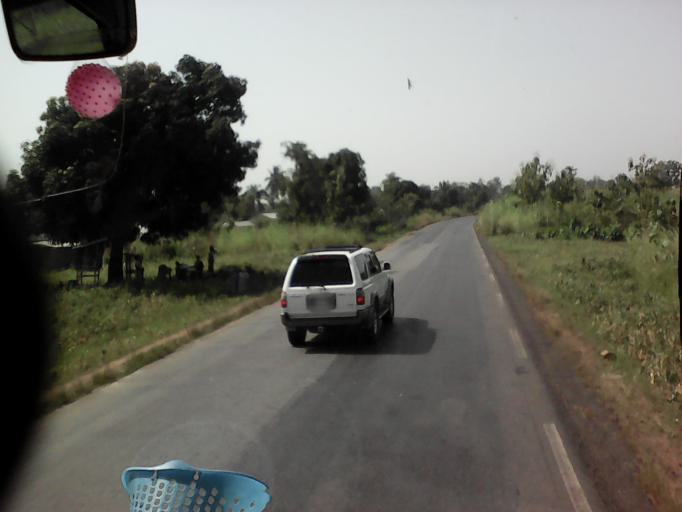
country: TG
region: Centrale
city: Sokode
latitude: 8.7762
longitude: 1.0639
